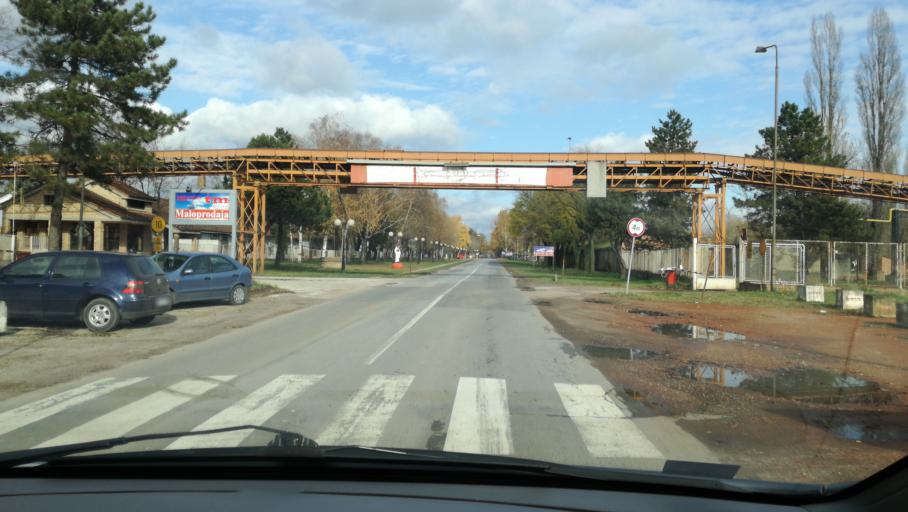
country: RS
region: Autonomna Pokrajina Vojvodina
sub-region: Severnobanatski Okrug
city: Kikinda
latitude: 45.8074
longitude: 20.4455
